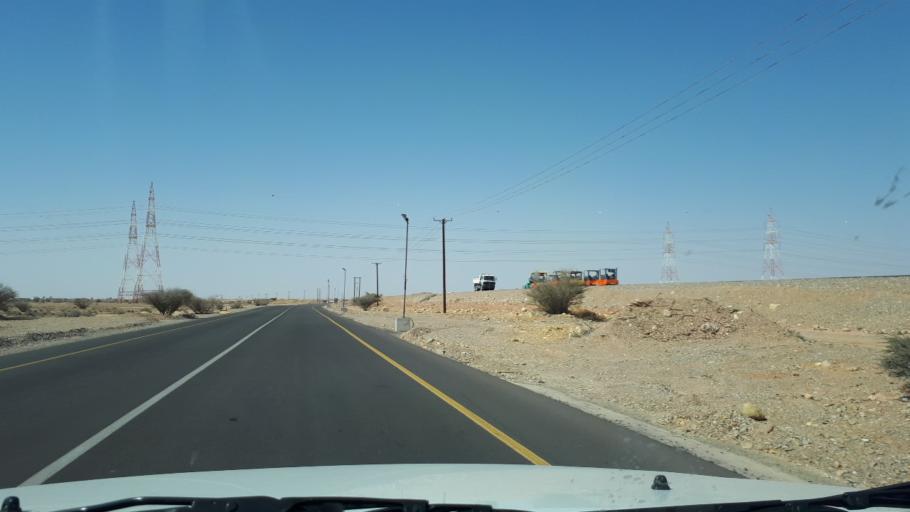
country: OM
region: Ash Sharqiyah
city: Sur
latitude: 22.2866
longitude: 59.2732
